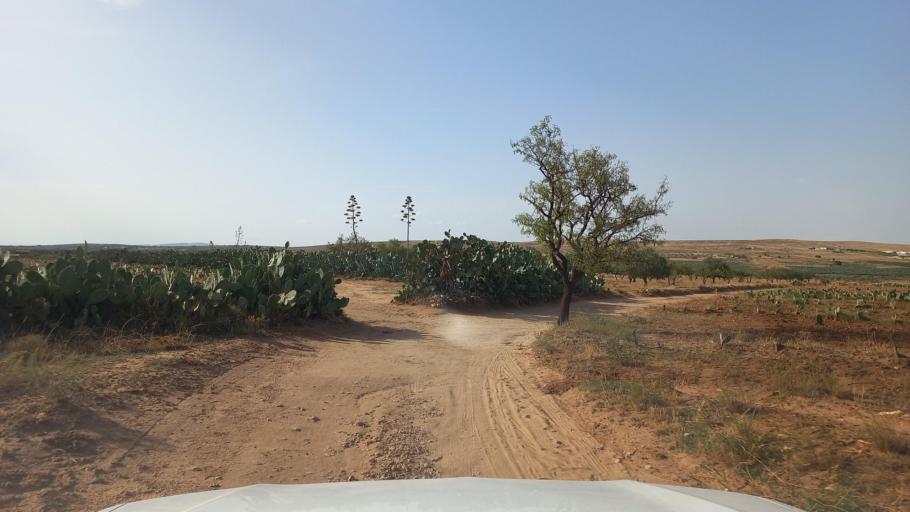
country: TN
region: Al Qasrayn
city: Kasserine
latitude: 35.3503
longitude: 8.8487
